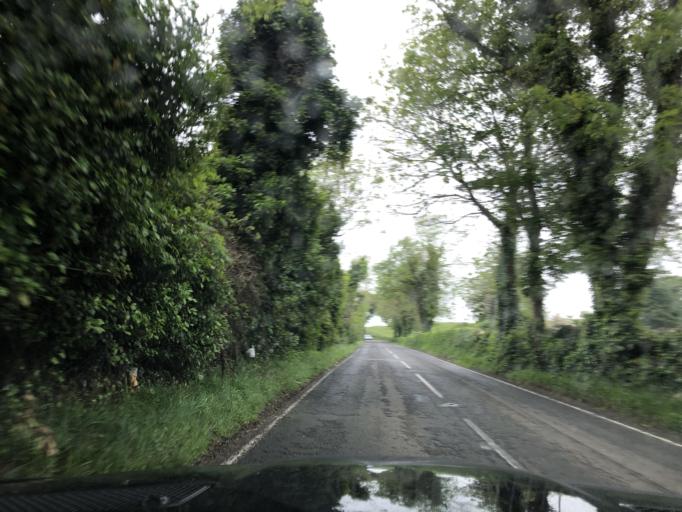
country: GB
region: Northern Ireland
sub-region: Down District
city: Portaferry
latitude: 54.3620
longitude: -5.5702
